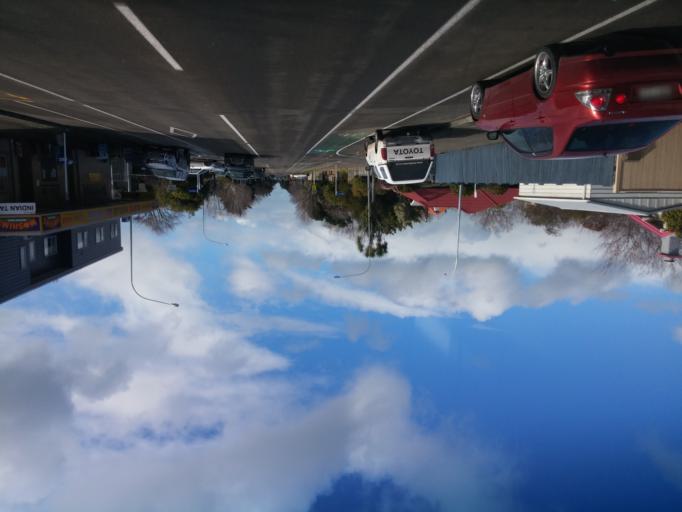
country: NZ
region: Manawatu-Wanganui
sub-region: Palmerston North City
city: Palmerston North
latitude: -40.3607
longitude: 175.6191
